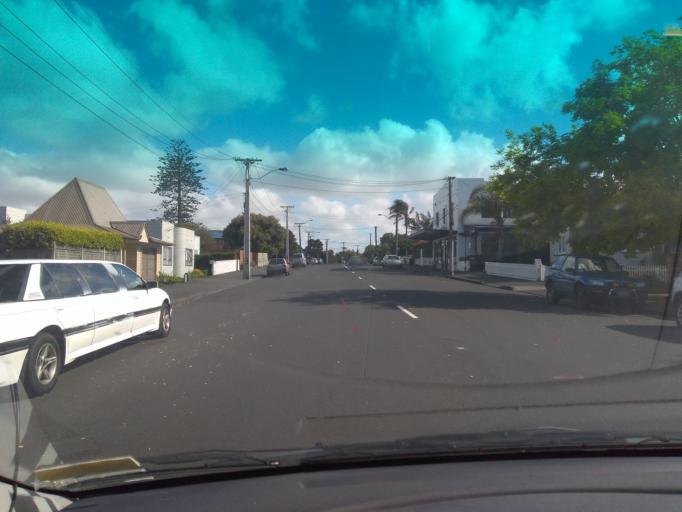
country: NZ
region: Auckland
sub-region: Auckland
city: Rosebank
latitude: -36.8530
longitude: 174.7042
